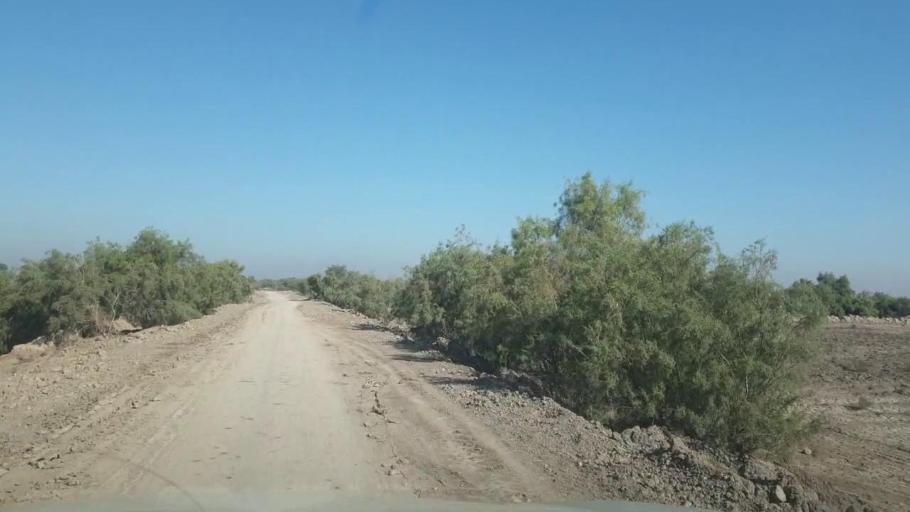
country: PK
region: Sindh
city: Bhan
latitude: 26.5431
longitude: 67.6544
